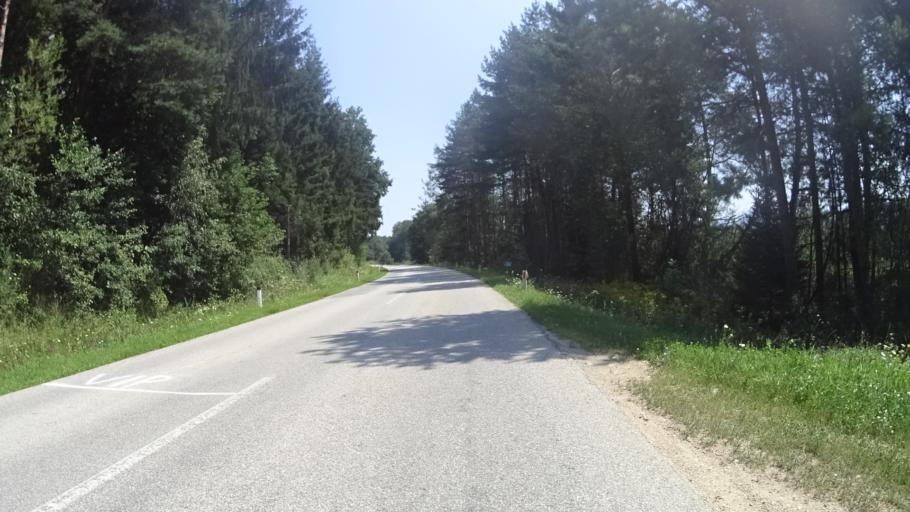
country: AT
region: Carinthia
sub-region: Politischer Bezirk Volkermarkt
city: Bleiburg/Pliberk
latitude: 46.5688
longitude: 14.8192
